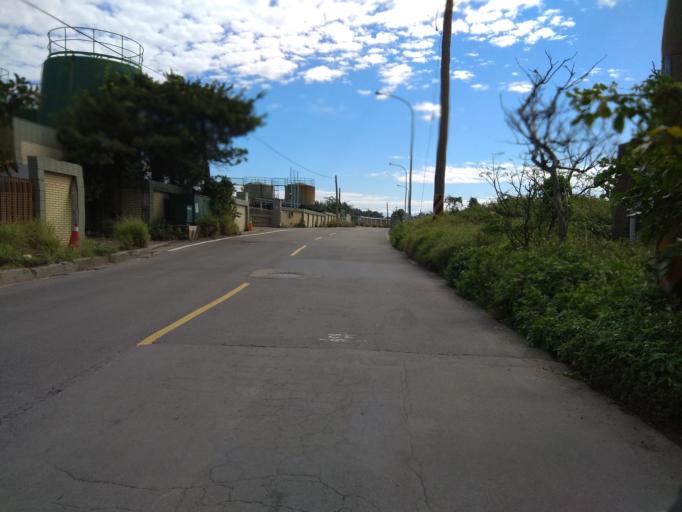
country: TW
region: Taiwan
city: Taoyuan City
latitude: 25.0642
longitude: 121.1280
